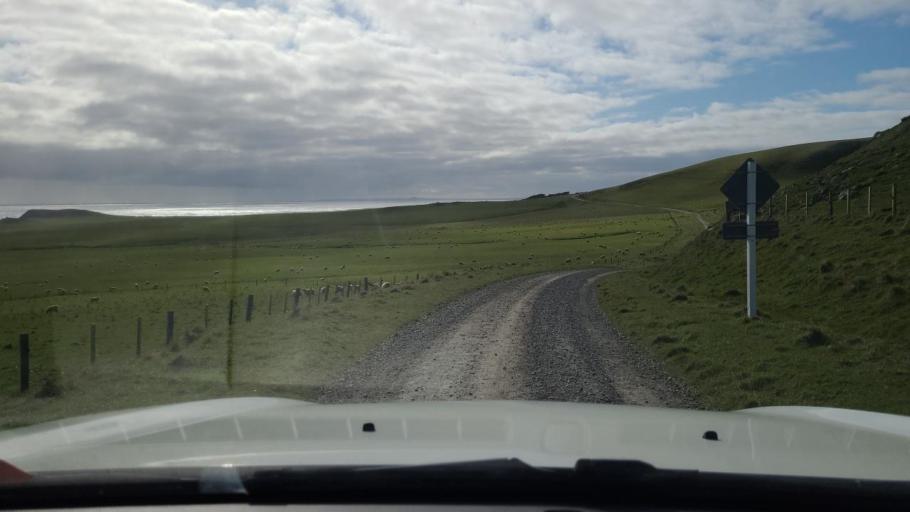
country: NZ
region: Chatham Islands
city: Waitangi
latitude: -44.0272
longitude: -176.6663
